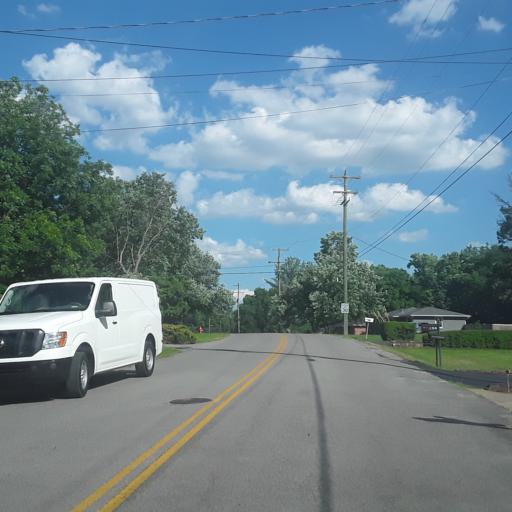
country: US
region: Tennessee
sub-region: Davidson County
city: Lakewood
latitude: 36.2044
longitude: -86.6371
